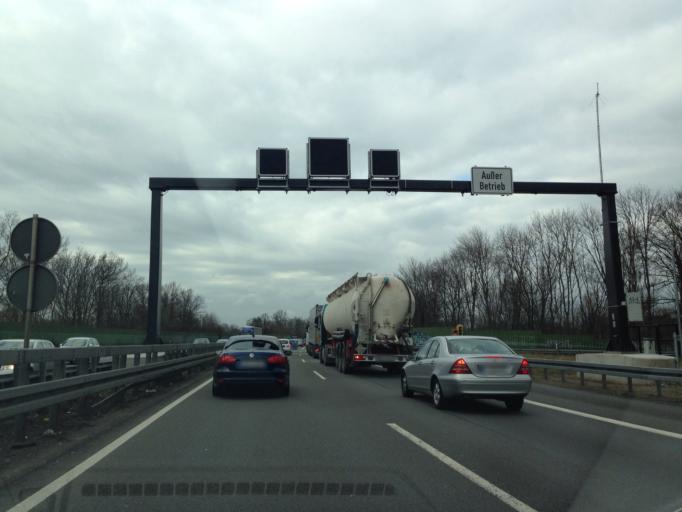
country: DE
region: North Rhine-Westphalia
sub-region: Regierungsbezirk Arnsberg
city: Herne
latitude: 51.5153
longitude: 7.2144
